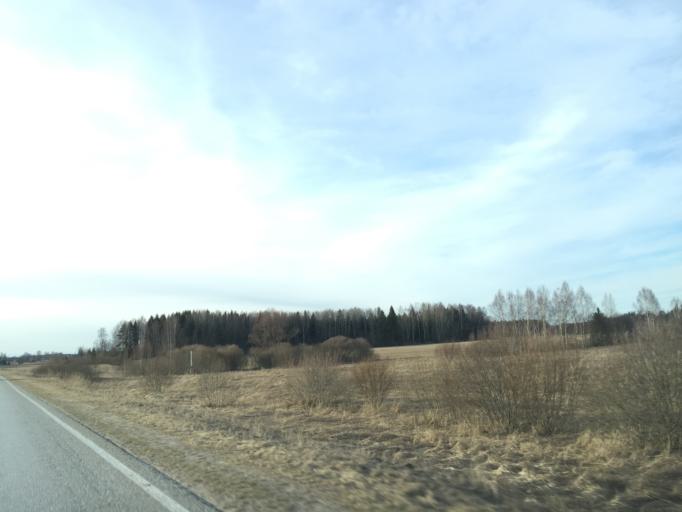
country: LV
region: Krimulda
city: Ragana
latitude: 57.1701
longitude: 24.7354
